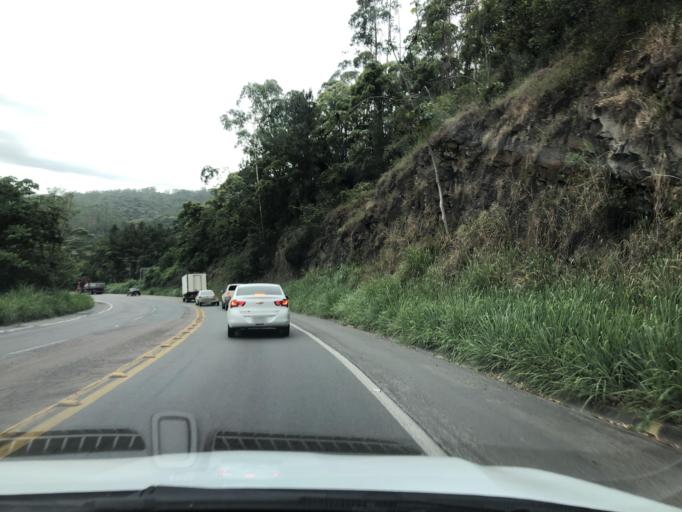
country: BR
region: Santa Catarina
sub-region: Ibirama
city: Ibirama
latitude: -27.0880
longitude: -49.5190
